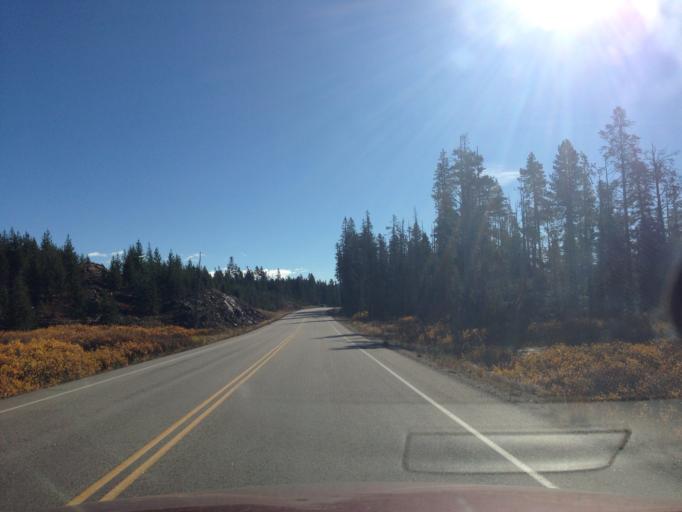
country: US
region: Montana
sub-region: Carbon County
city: Red Lodge
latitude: 45.0265
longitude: -109.8887
